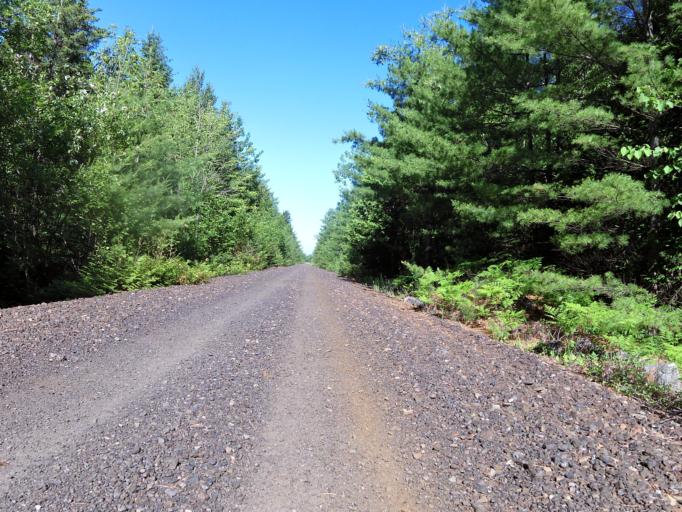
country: CA
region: Ontario
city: Arnprior
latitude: 45.4595
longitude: -76.2260
